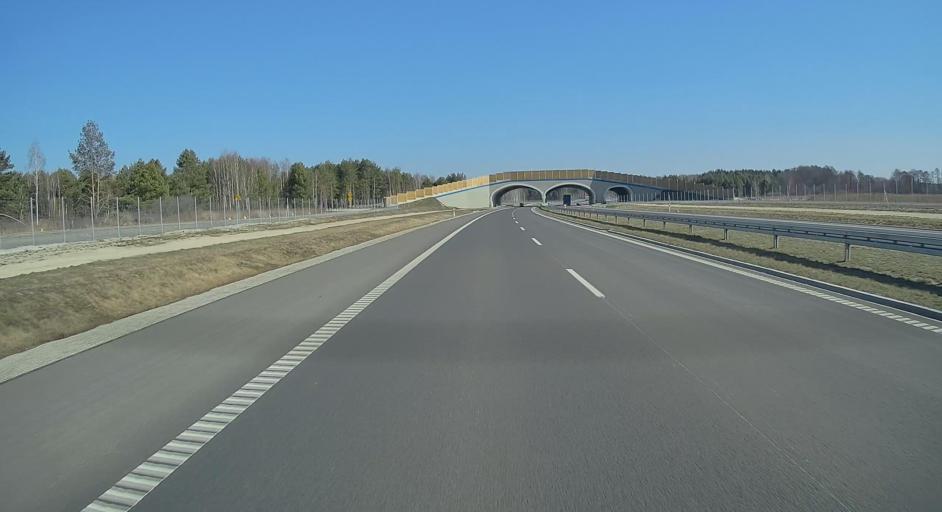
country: PL
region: Subcarpathian Voivodeship
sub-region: Powiat nizanski
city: Jarocin
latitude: 50.5939
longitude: 22.2610
